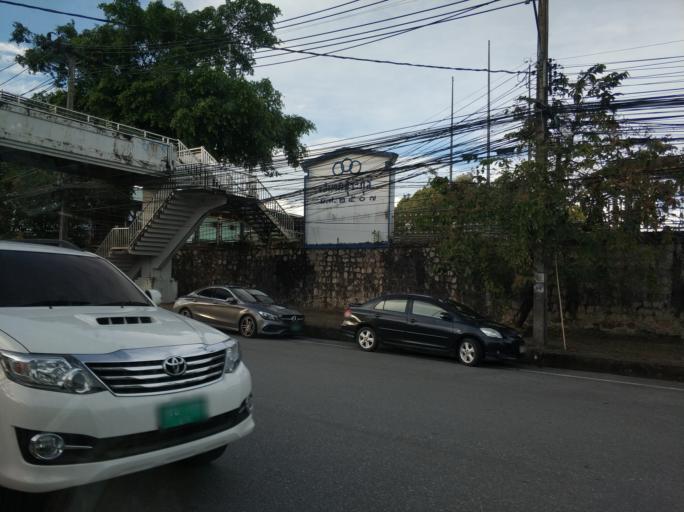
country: TH
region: Phuket
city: Wichit
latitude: 7.8879
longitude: 98.3716
